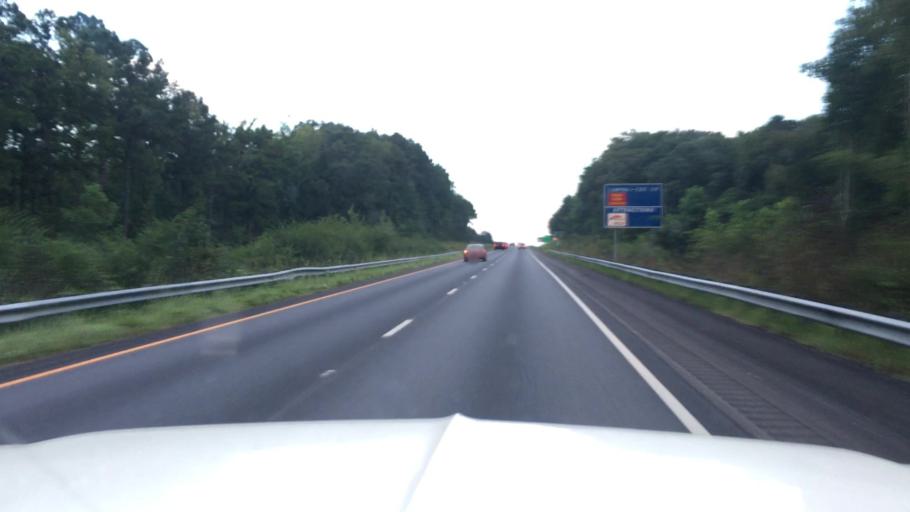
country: US
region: Alabama
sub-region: Chilton County
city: Jemison
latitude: 32.9902
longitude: -86.6956
